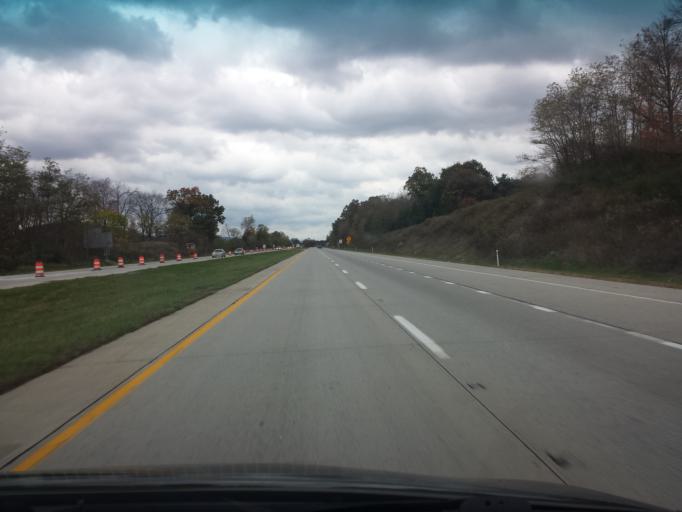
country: US
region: Pennsylvania
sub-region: Blair County
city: Bellwood
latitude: 40.6053
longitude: -78.3109
